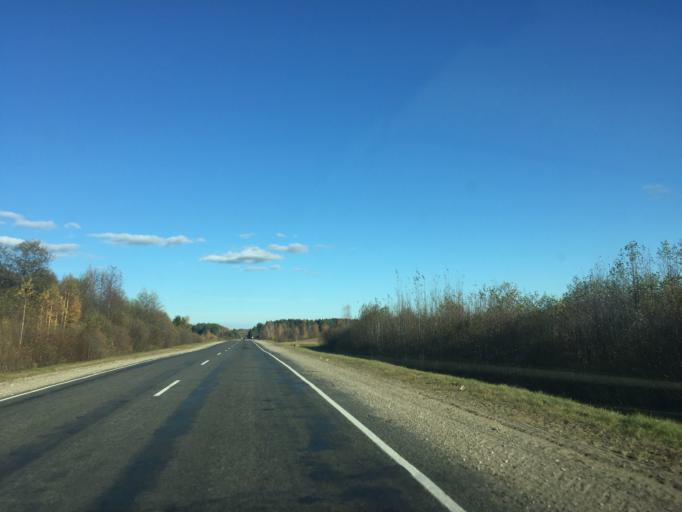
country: BY
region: Vitebsk
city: Dzisna
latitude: 55.2431
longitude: 28.0769
